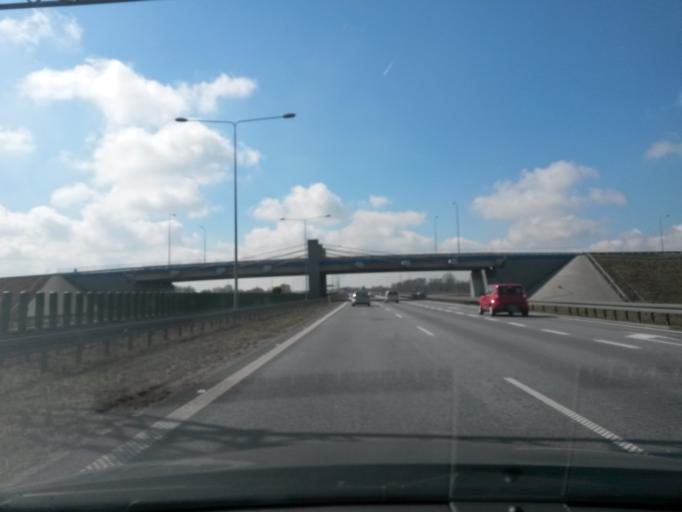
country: PL
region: Lodz Voivodeship
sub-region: powiat Lowicki
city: Nieborow
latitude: 52.0448
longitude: 20.0533
